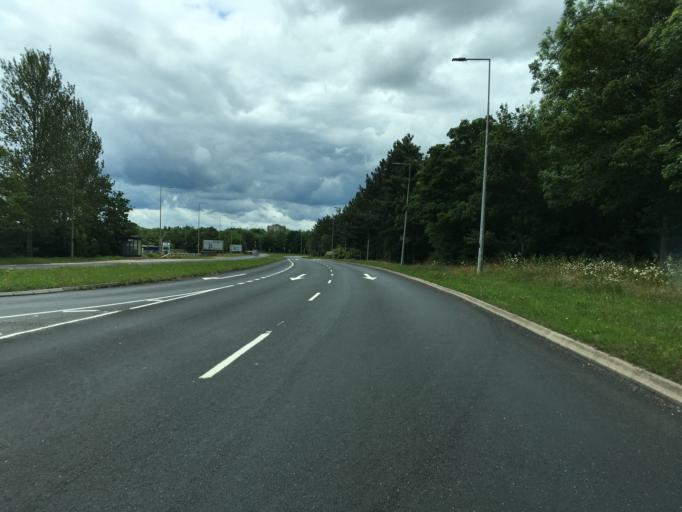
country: GB
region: England
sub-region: Buckinghamshire
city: Bletchley
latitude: 52.0149
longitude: -0.7360
